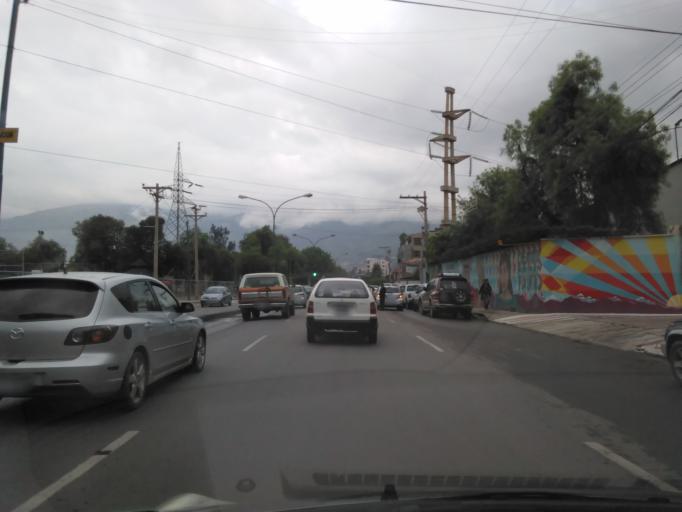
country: BO
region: Cochabamba
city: Cochabamba
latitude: -17.3931
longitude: -66.1662
